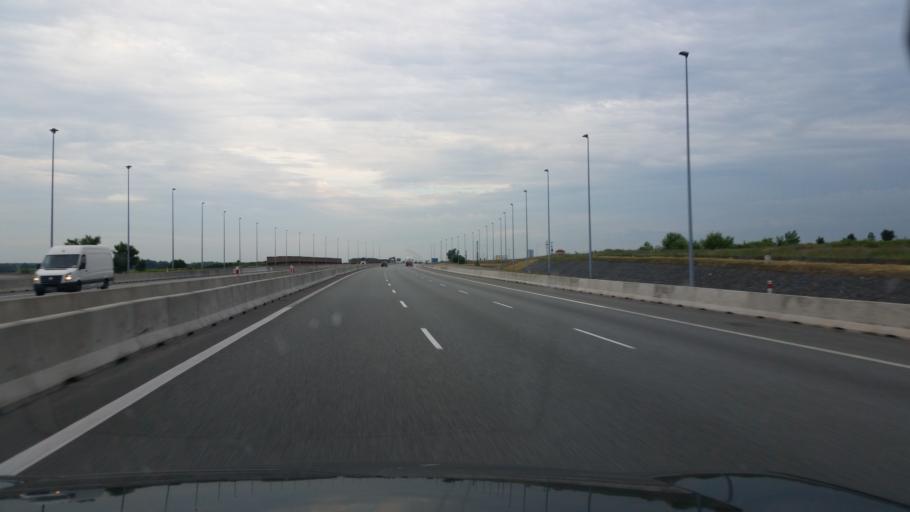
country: PL
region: Silesian Voivodeship
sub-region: Powiat gliwicki
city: Gieraltowice
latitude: 50.2396
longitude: 18.7088
